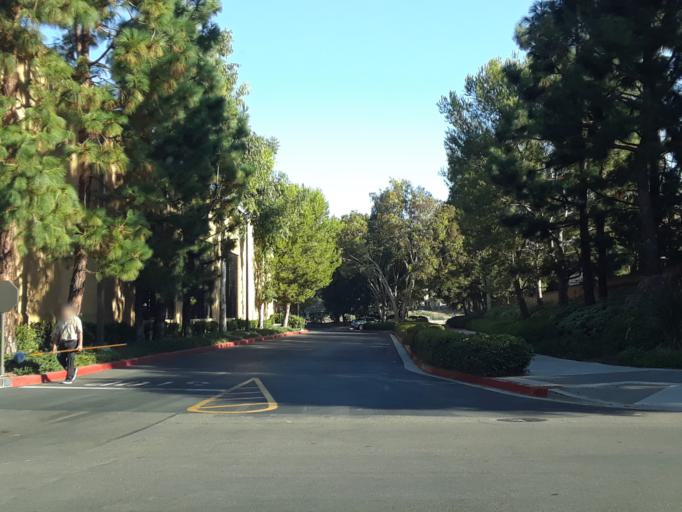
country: US
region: California
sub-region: Orange County
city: Irvine
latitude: 33.6692
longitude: -117.7846
